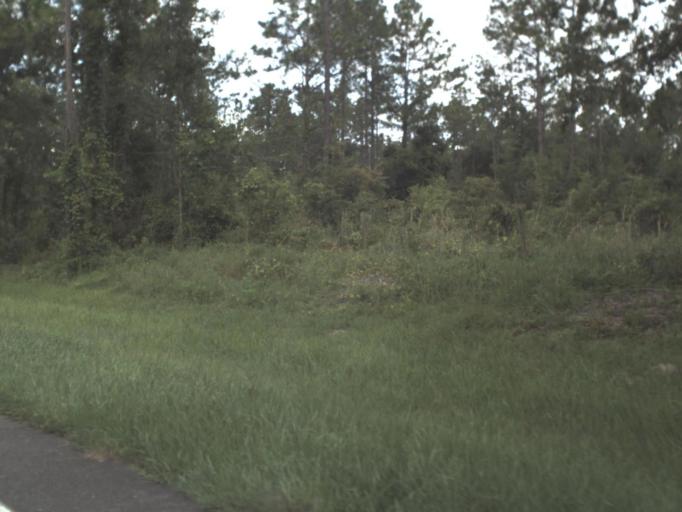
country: US
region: Florida
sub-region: Alachua County
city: Archer
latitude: 29.4627
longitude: -82.4781
